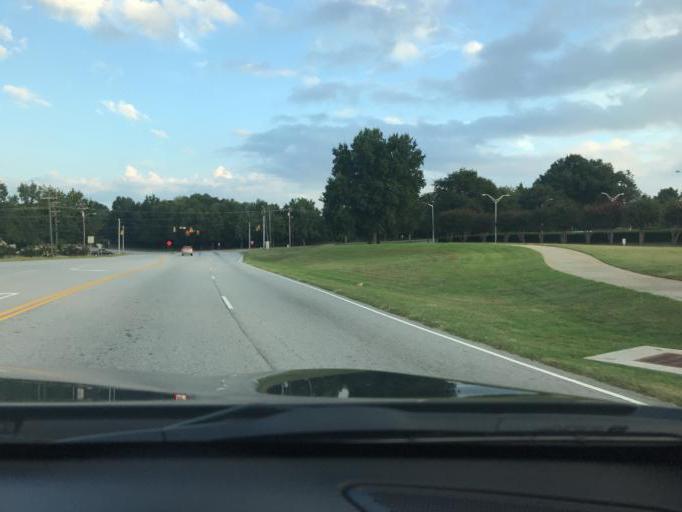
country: US
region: South Carolina
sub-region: Greenville County
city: Dunean
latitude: 34.8166
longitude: -82.4144
